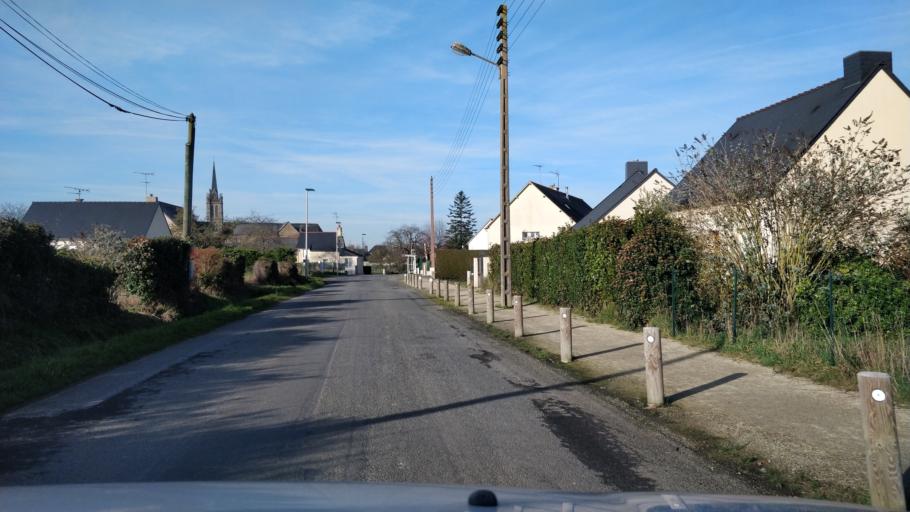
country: FR
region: Brittany
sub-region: Departement d'Ille-et-Vilaine
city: Plerguer
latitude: 48.5257
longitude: -1.8449
